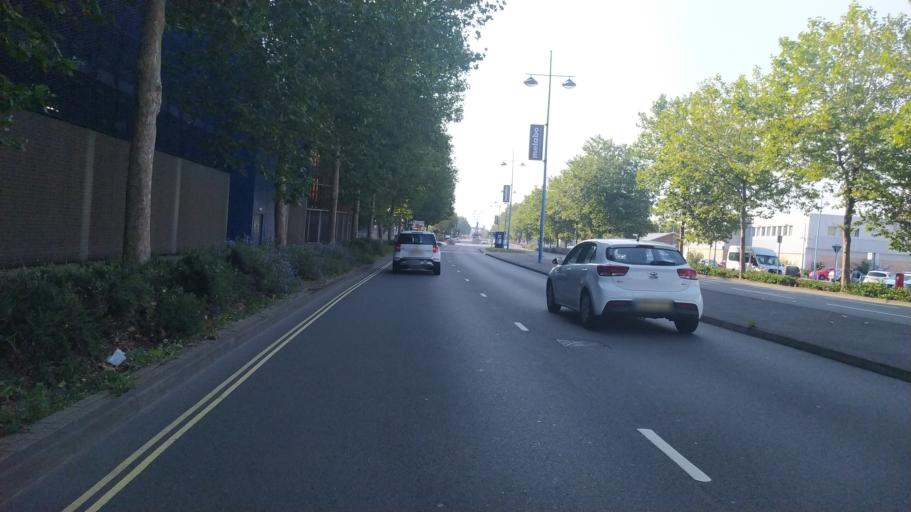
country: GB
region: England
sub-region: Southampton
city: Southampton
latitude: 50.9025
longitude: -1.4109
